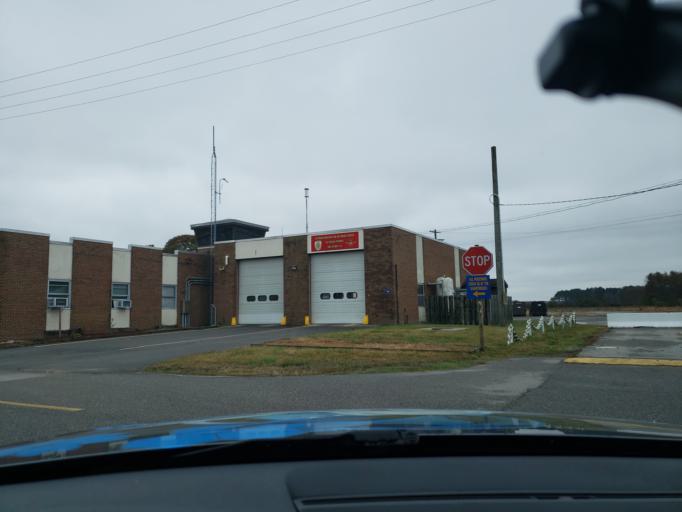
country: US
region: Virginia
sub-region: City of Chesapeake
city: Chesapeake
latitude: 36.7061
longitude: -76.1287
